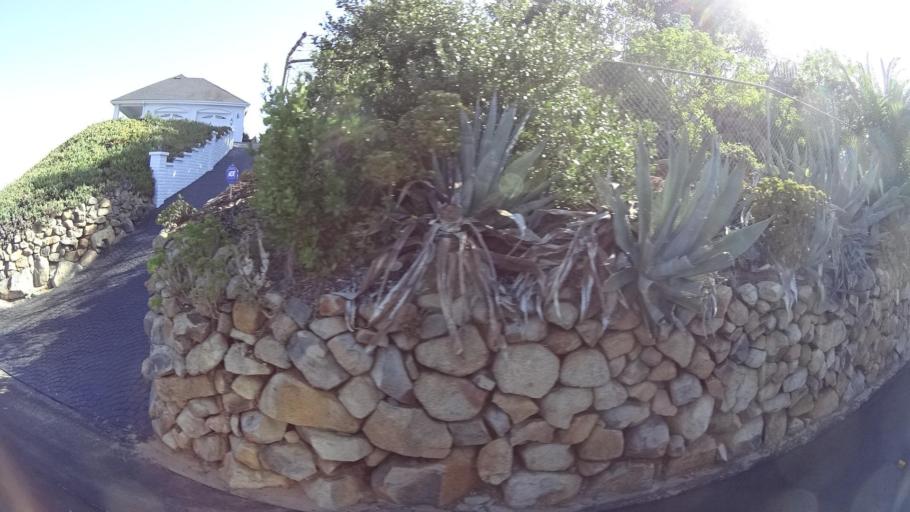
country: US
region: California
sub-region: San Diego County
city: Casa de Oro-Mount Helix
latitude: 32.7700
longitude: -116.9825
